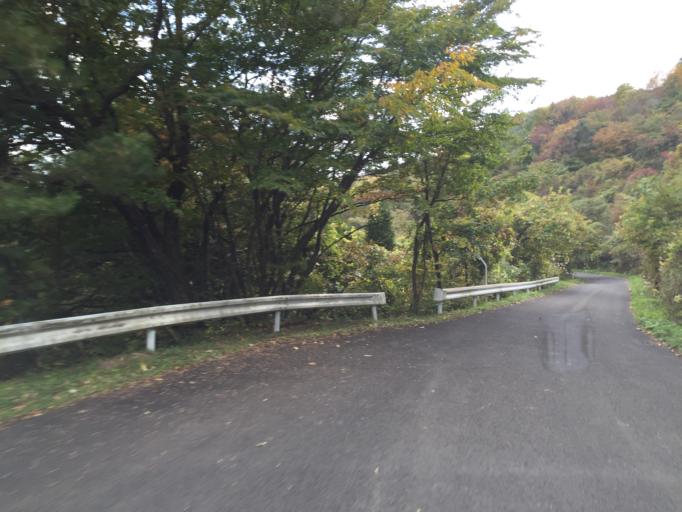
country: JP
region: Fukushima
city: Fukushima-shi
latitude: 37.7086
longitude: 140.3335
